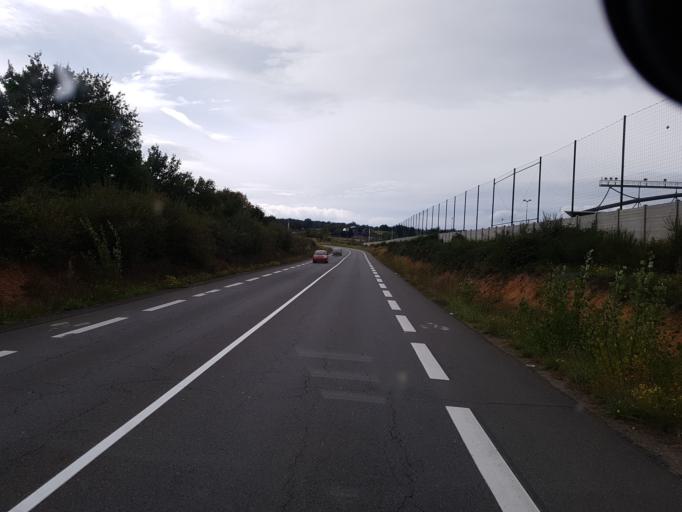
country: FR
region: Rhone-Alpes
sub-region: Departement de la Loire
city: La Fouillouse
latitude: 45.5234
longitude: 4.3006
